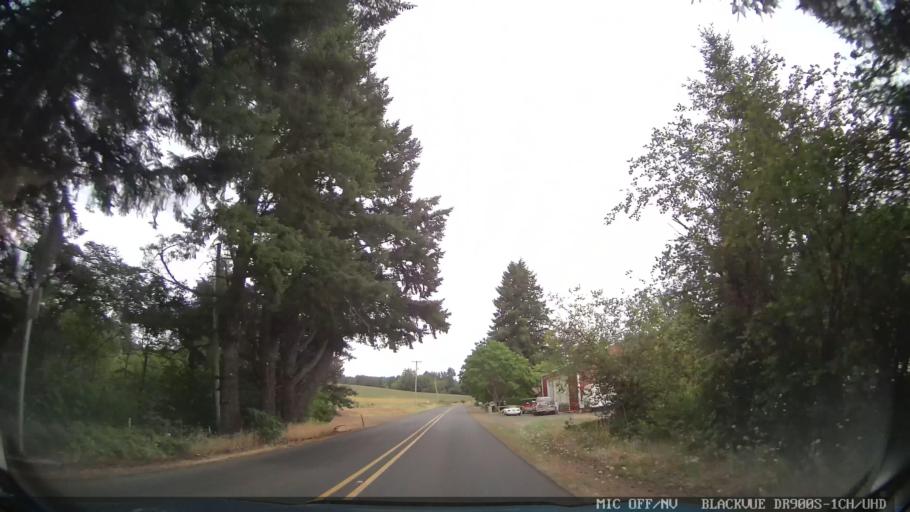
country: US
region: Oregon
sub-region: Linn County
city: Lyons
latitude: 44.8515
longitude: -122.6777
